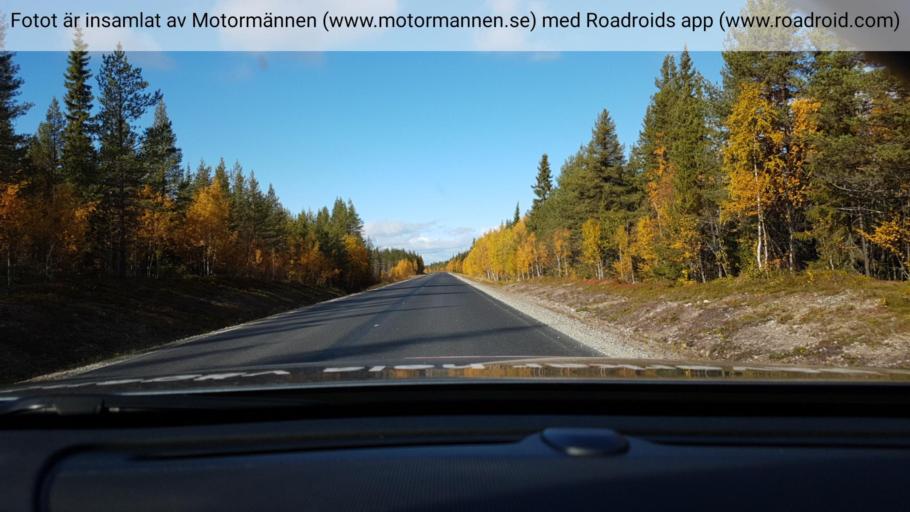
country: SE
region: Norrbotten
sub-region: Arjeplogs Kommun
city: Arjeplog
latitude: 65.9708
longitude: 18.2546
